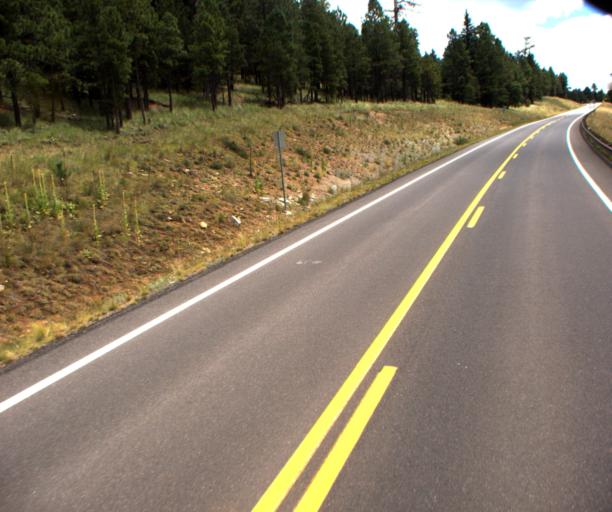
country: US
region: Arizona
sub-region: Apache County
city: Eagar
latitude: 33.9620
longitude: -109.5042
